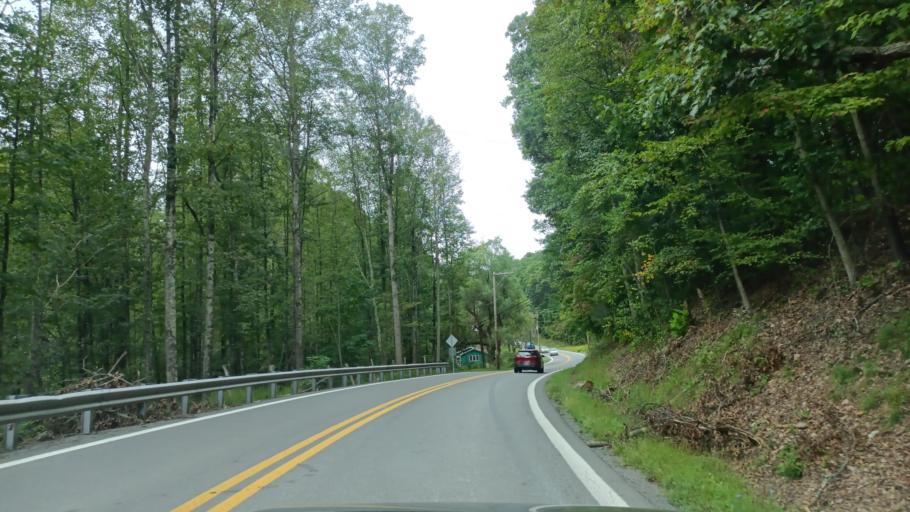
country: US
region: West Virginia
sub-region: Taylor County
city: Grafton
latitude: 39.3293
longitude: -79.9123
